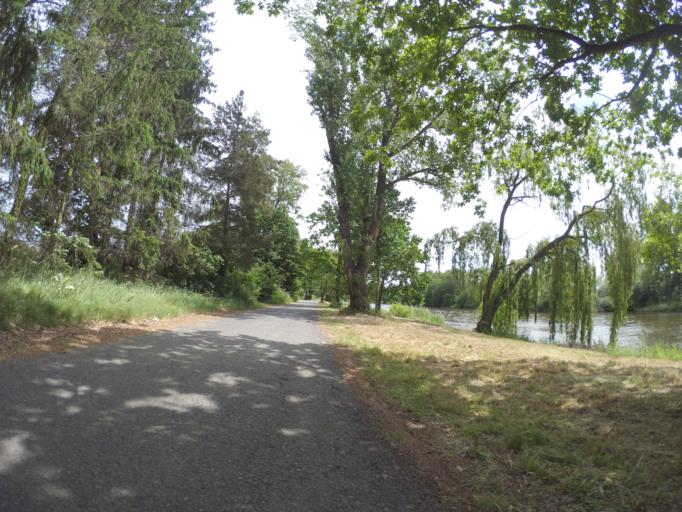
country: CZ
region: Central Bohemia
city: Lysa nad Labem
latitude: 50.1721
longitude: 14.8773
